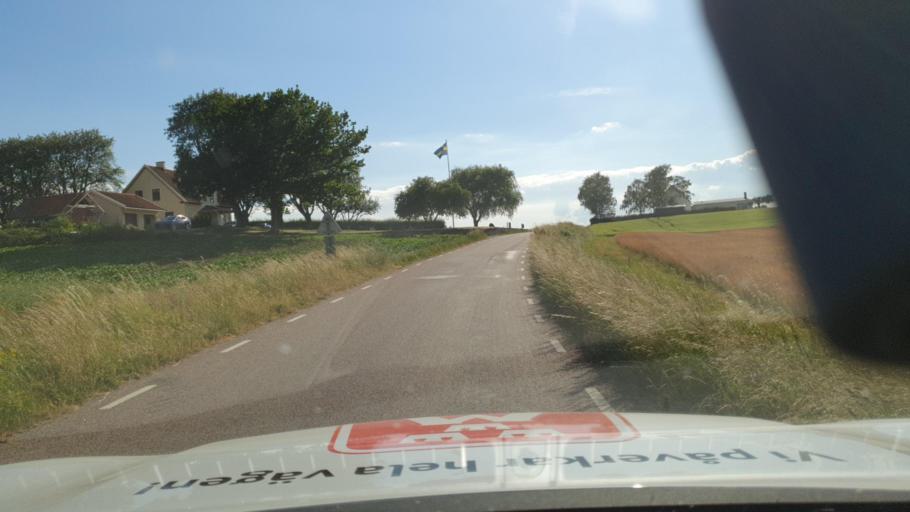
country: SE
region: Skane
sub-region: Ystads Kommun
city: Ystad
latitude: 55.4467
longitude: 13.7077
